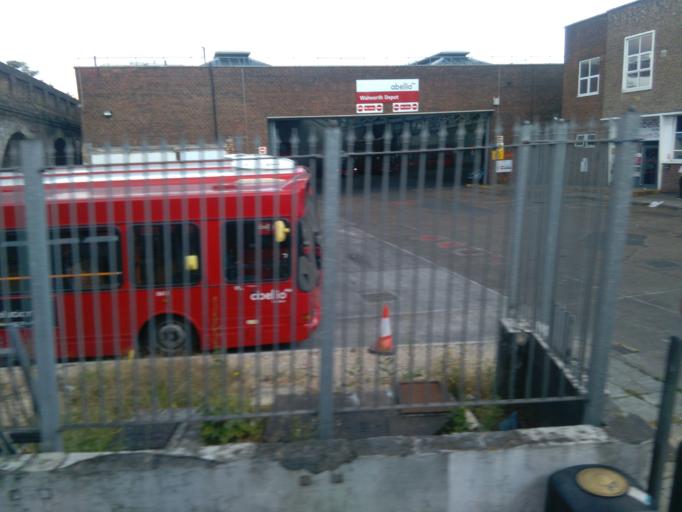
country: GB
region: England
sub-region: Greater London
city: Camberwell
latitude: 51.4754
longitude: -0.0963
